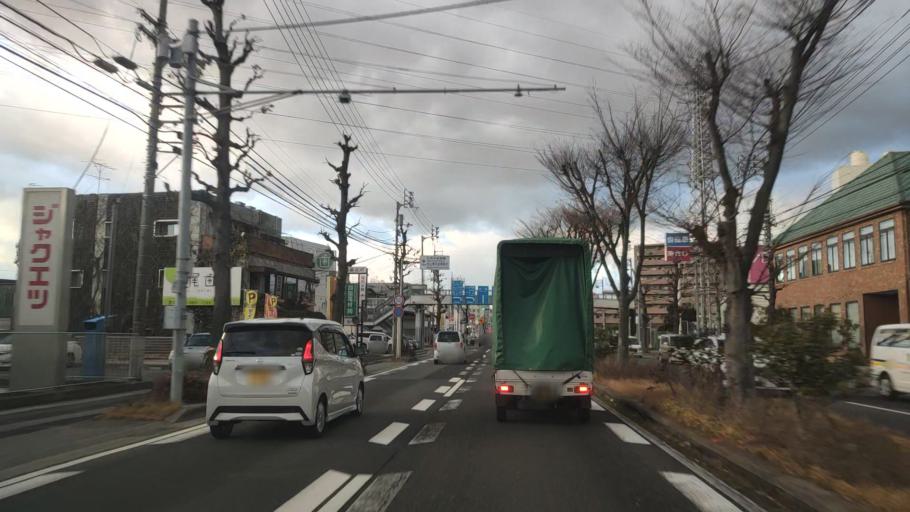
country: JP
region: Ehime
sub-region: Shikoku-chuo Shi
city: Matsuyama
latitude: 33.8199
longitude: 132.7766
